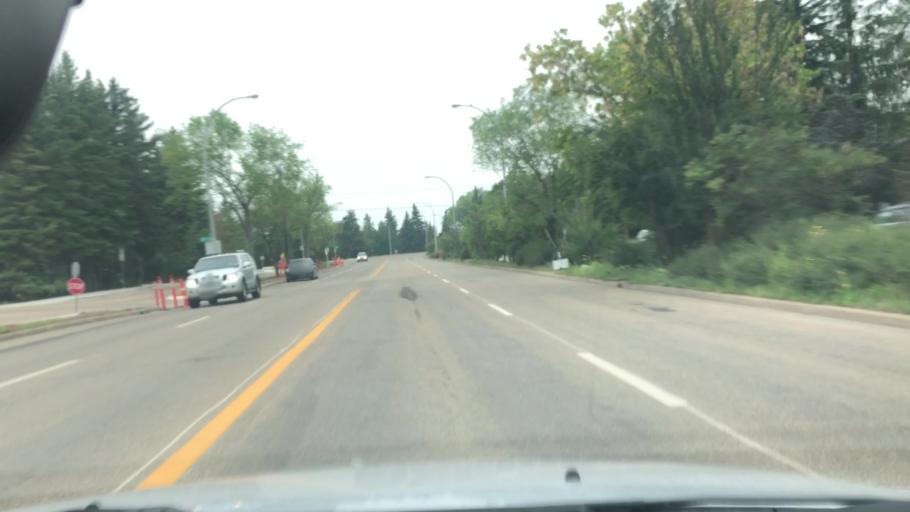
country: CA
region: Alberta
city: Edmonton
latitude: 53.5179
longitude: -113.5339
